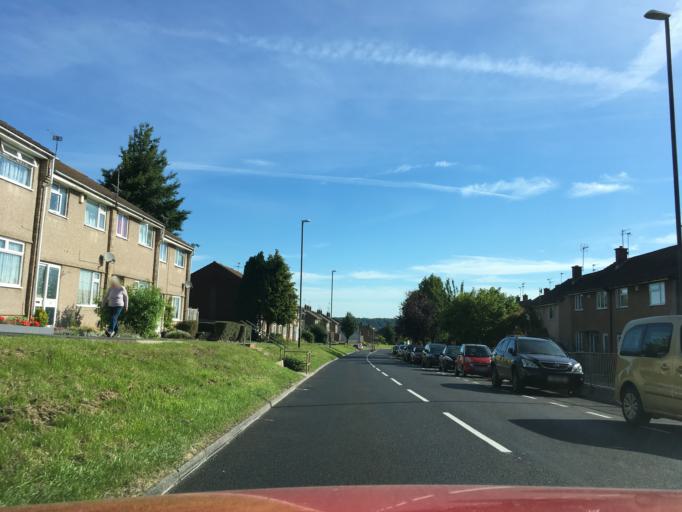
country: GB
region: England
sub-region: Bath and North East Somerset
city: Keynsham
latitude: 51.4090
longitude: -2.5138
